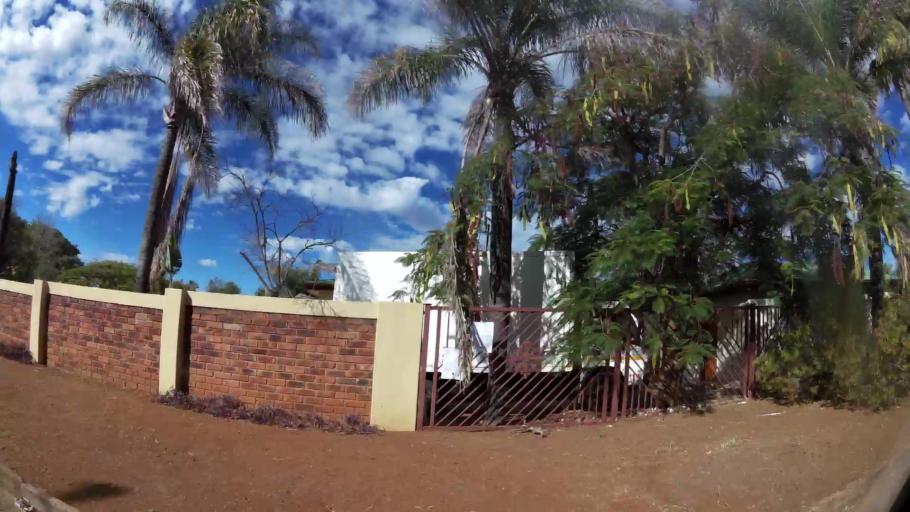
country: ZA
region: Limpopo
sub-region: Waterberg District Municipality
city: Bela-Bela
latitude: -24.8780
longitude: 28.2902
